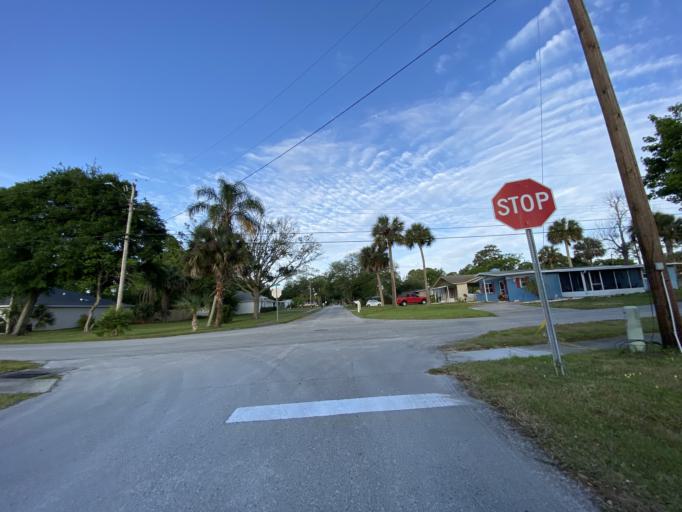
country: US
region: Florida
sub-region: Volusia County
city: South Daytona
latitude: 29.1753
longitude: -81.0088
